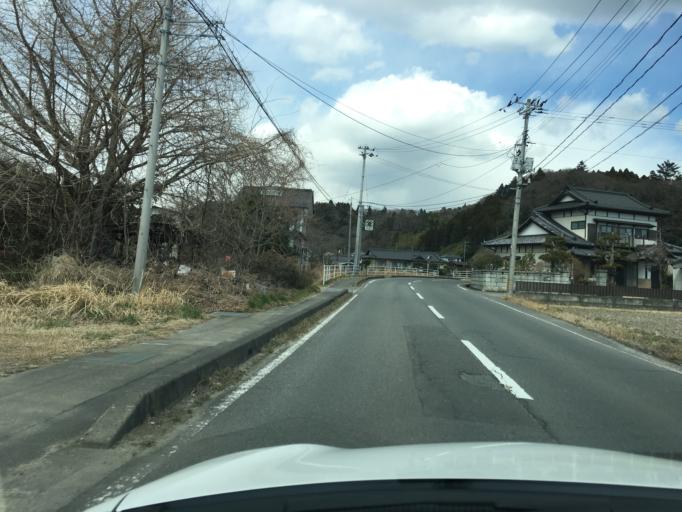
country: JP
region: Fukushima
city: Iwaki
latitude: 37.0622
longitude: 140.9109
